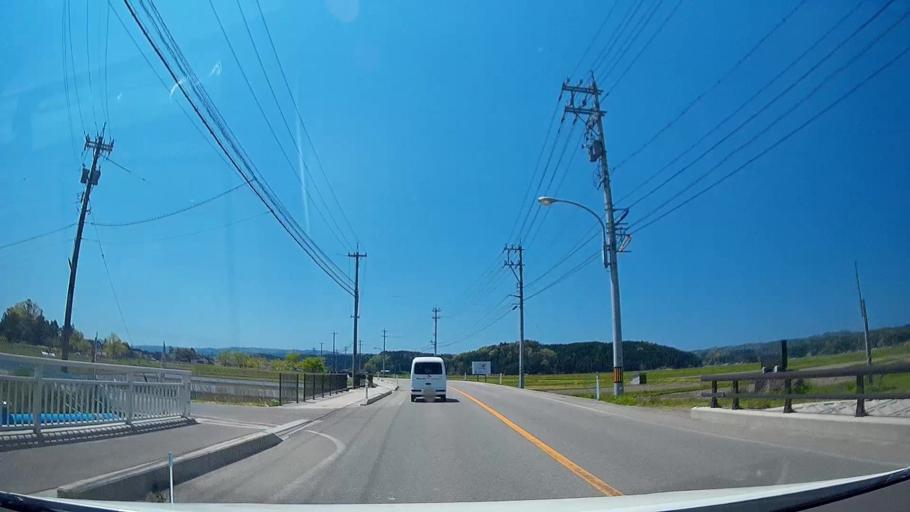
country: JP
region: Ishikawa
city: Nanao
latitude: 37.4503
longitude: 137.2940
